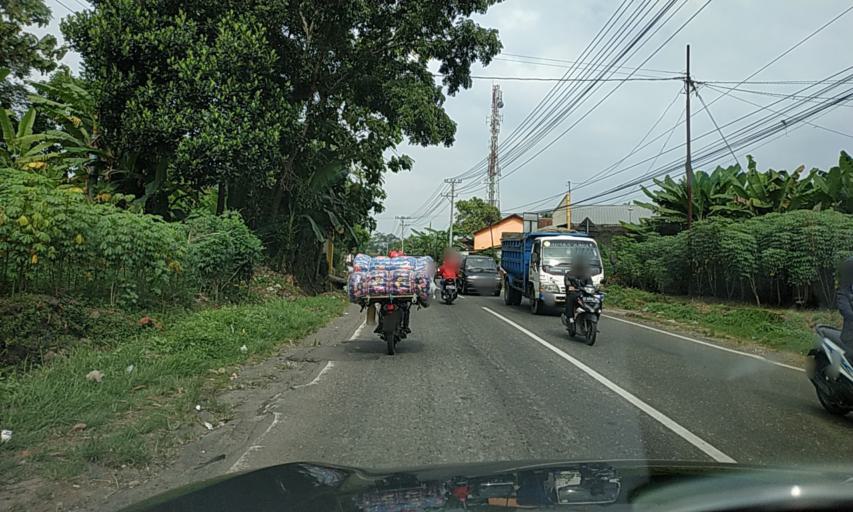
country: ID
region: Central Java
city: Purwokerto
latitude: -7.4183
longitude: 109.1918
